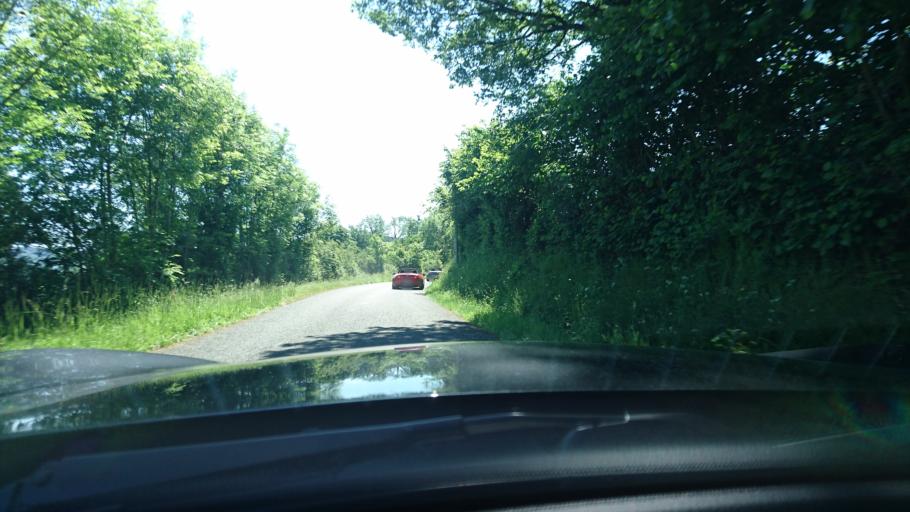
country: FR
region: Rhone-Alpes
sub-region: Departement de la Loire
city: Bussieres
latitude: 45.8775
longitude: 4.2833
